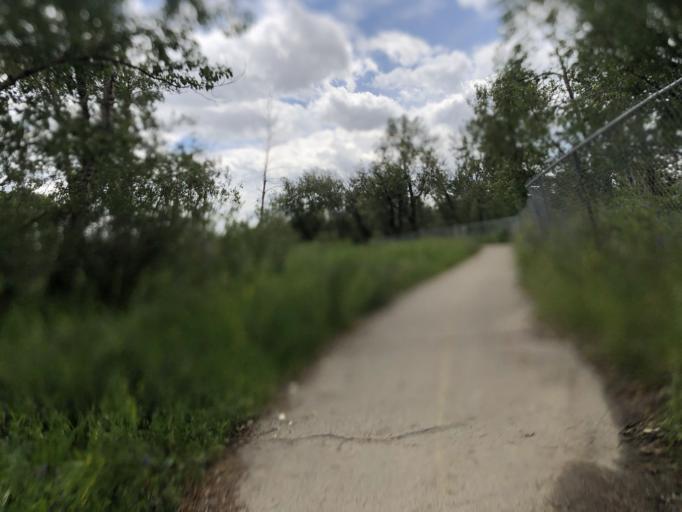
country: CA
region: Alberta
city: Calgary
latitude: 51.0058
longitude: -114.0201
